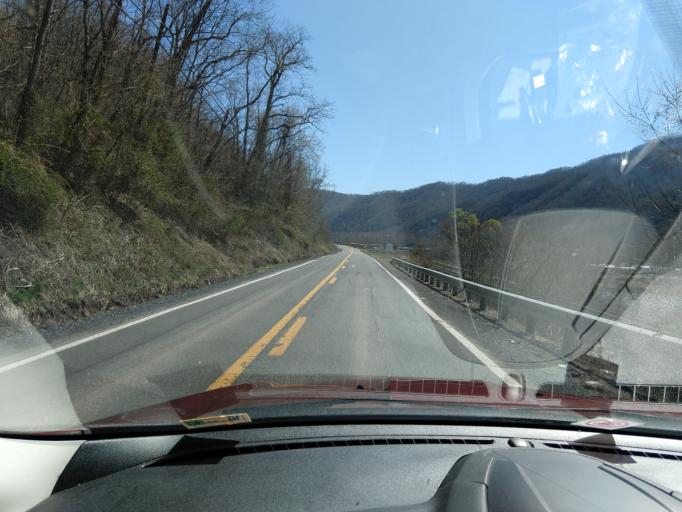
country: US
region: West Virginia
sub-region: Summers County
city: Hinton
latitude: 37.7113
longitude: -80.8877
